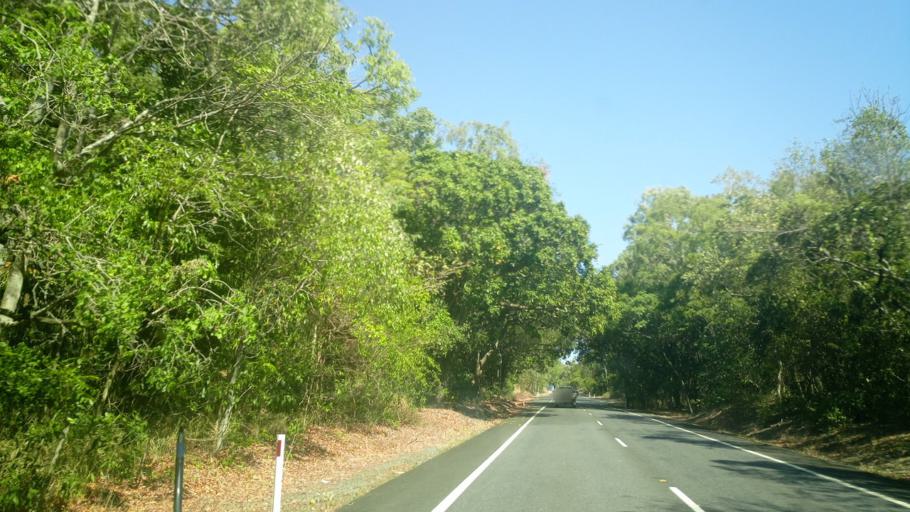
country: AU
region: Queensland
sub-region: Cairns
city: Palm Cove
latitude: -16.7337
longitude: 145.6583
